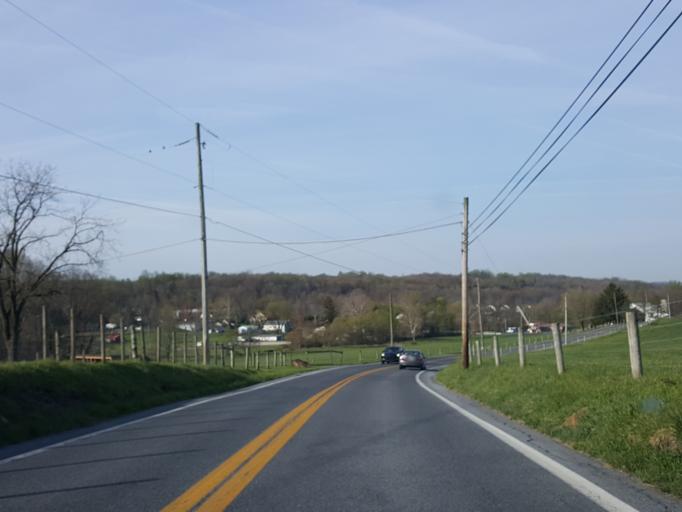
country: US
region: Pennsylvania
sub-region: Lebanon County
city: Campbelltown
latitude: 40.2448
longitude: -76.5082
